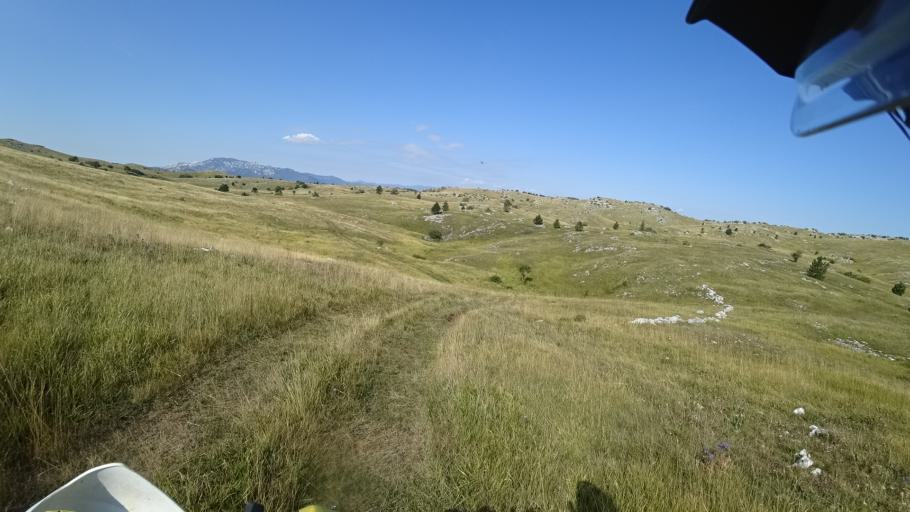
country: HR
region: Zadarska
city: Gracac
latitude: 44.3114
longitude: 15.9869
